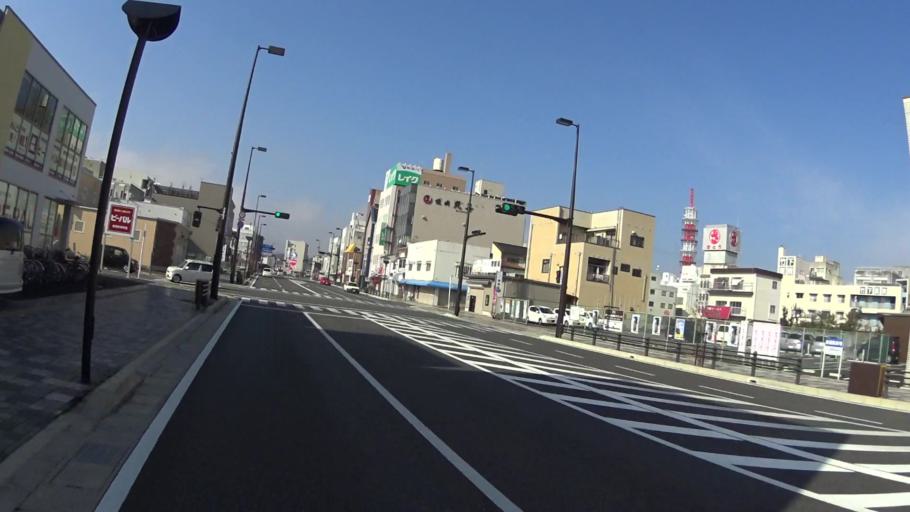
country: JP
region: Kyoto
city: Fukuchiyama
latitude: 35.2972
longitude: 135.1209
